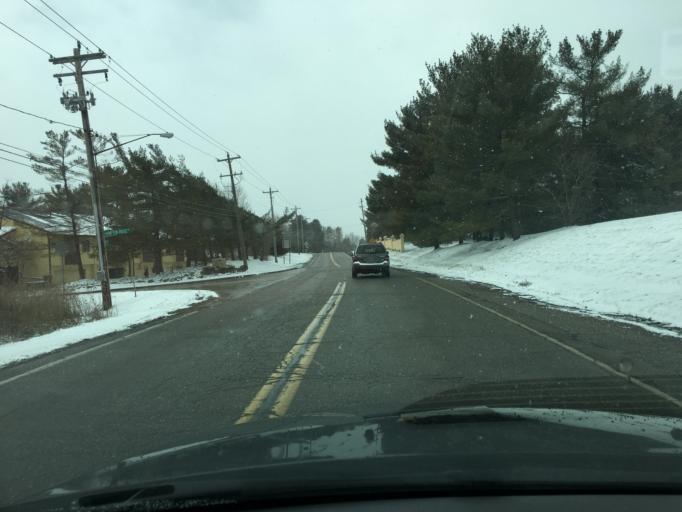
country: US
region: Ohio
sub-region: Summit County
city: Fairlawn
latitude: 41.1409
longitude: -81.5776
